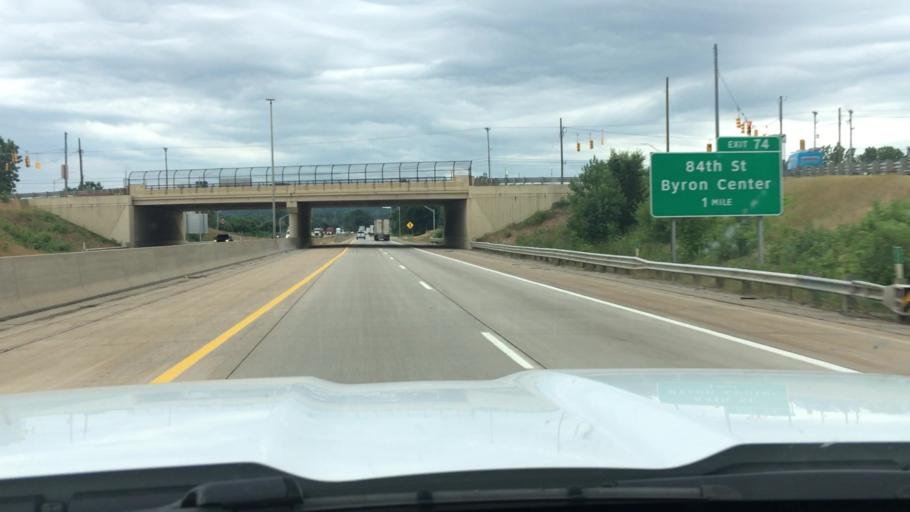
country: US
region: Michigan
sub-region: Kent County
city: Cutlerville
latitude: 42.8272
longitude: -85.6726
